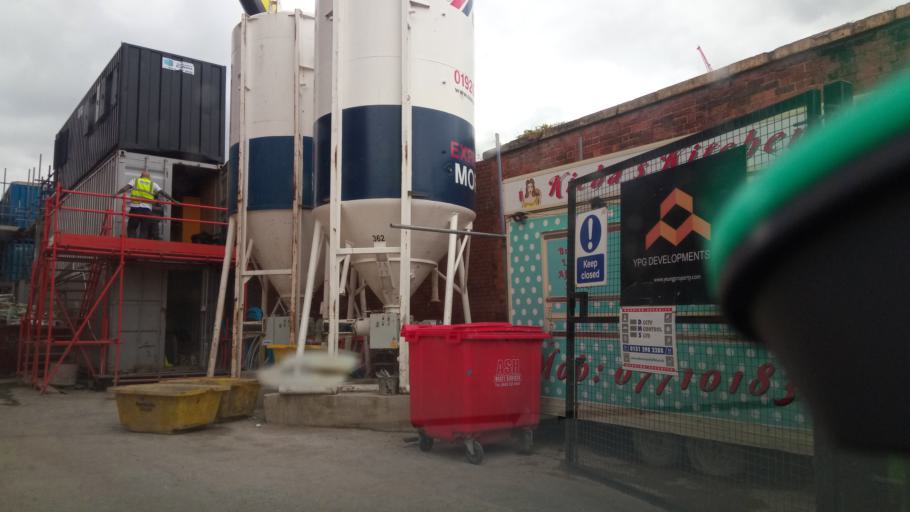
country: GB
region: England
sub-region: Liverpool
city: Liverpool
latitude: 53.3979
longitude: -2.9852
